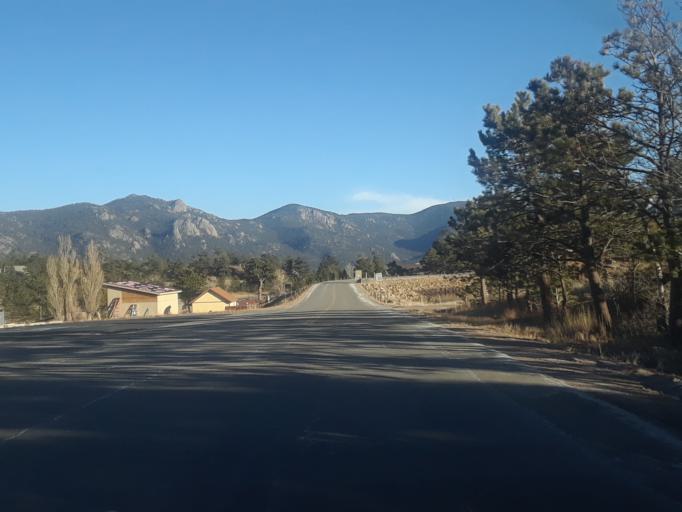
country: US
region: Colorado
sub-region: Larimer County
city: Estes Park
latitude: 40.3470
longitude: -105.5329
